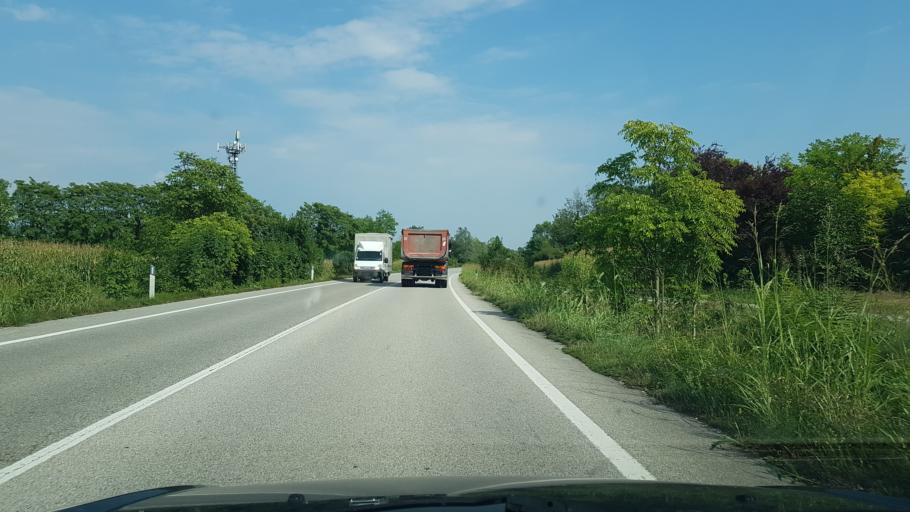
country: IT
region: Friuli Venezia Giulia
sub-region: Provincia di Pordenone
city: Spilimbergo
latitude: 46.0988
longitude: 12.8608
